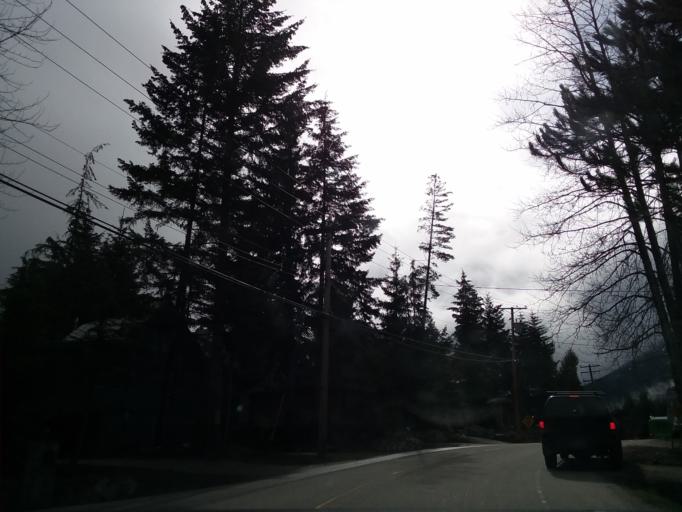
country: CA
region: British Columbia
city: Whistler
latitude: 50.1245
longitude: -122.9590
